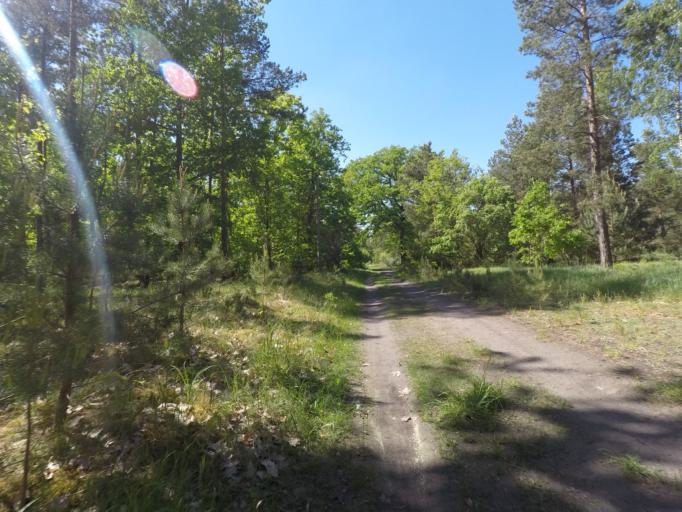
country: DE
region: Brandenburg
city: Eberswalde
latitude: 52.8156
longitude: 13.7660
